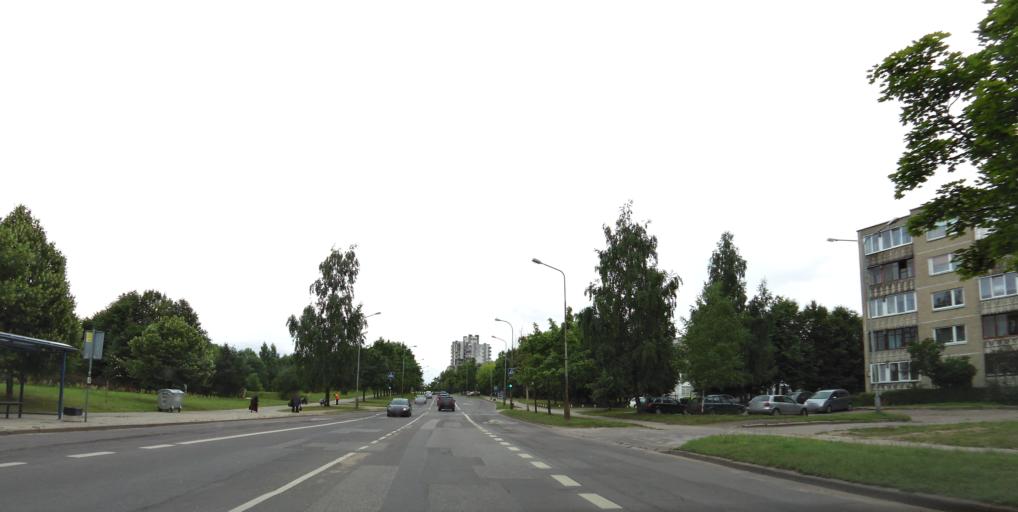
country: LT
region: Vilnius County
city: Seskine
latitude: 54.7153
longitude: 25.2574
